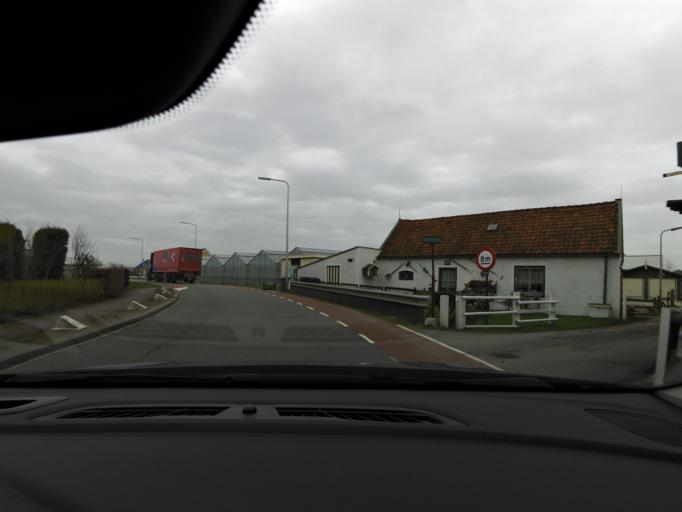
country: NL
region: South Holland
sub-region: Gemeente Westland
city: De Lier
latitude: 51.9712
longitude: 4.2425
